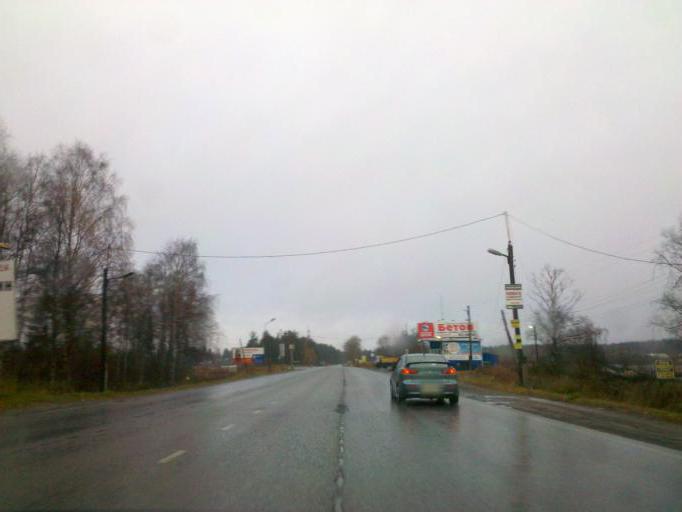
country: RU
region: Republic of Karelia
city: Petrozavodsk
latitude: 61.8225
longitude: 34.2696
